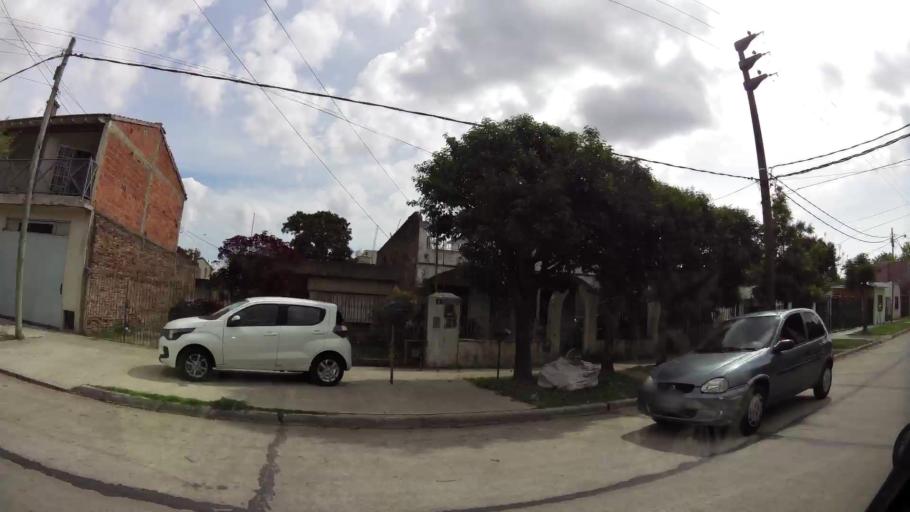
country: AR
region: Buenos Aires
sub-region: Partido de Quilmes
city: Quilmes
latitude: -34.7495
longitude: -58.2504
